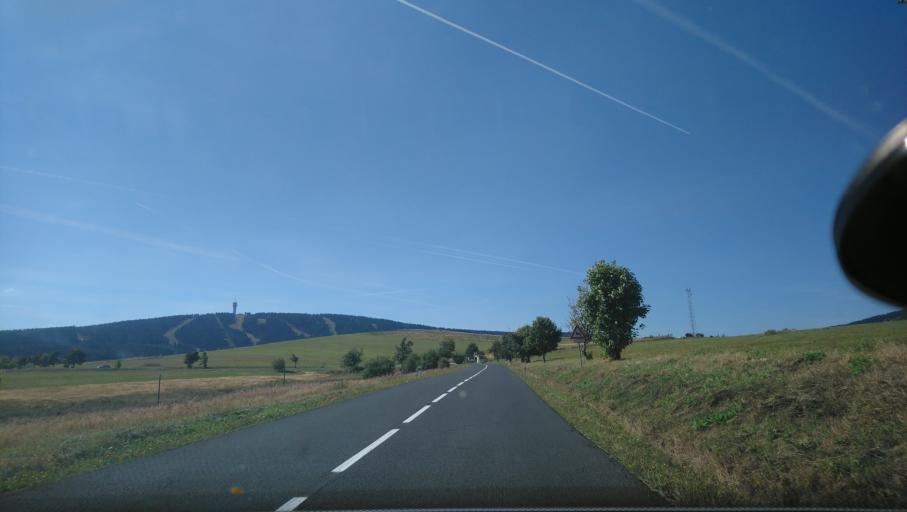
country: DE
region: Saxony
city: Kurort Oberwiesenthal
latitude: 50.4153
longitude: 12.9923
